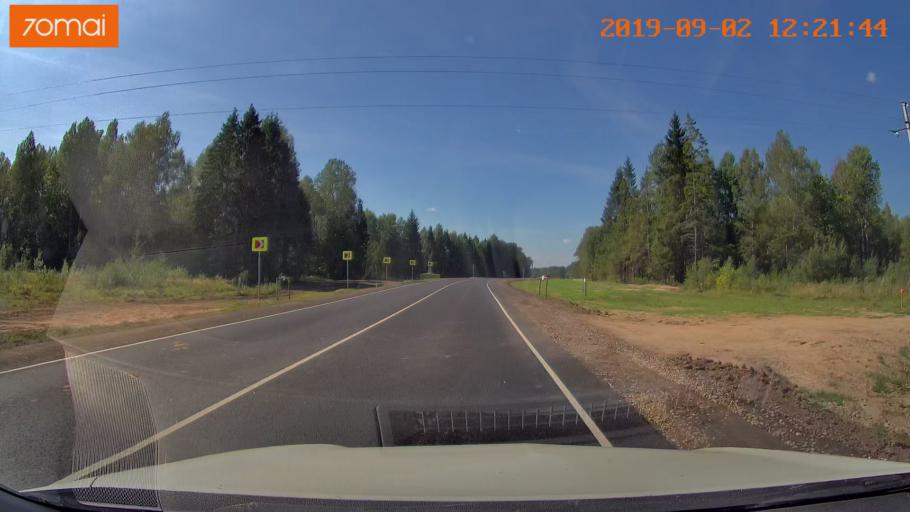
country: RU
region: Smolensk
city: Oster
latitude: 53.8857
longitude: 32.6496
